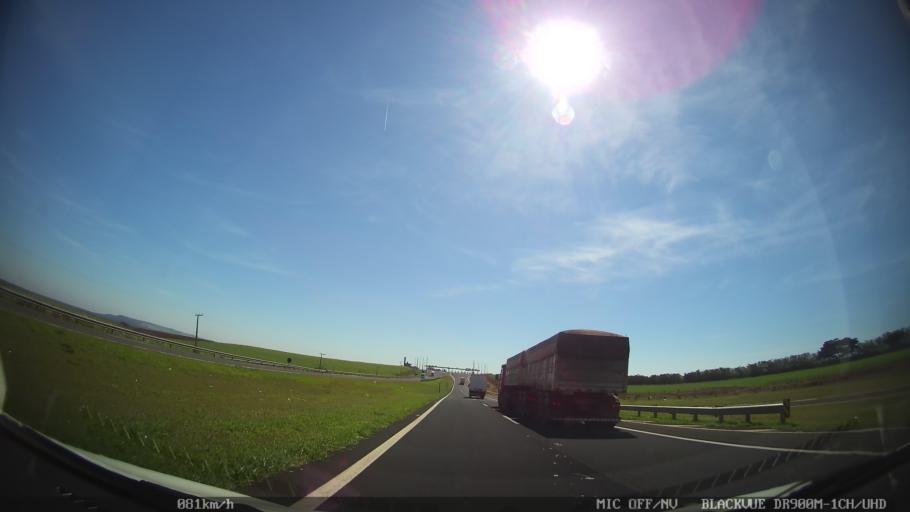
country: BR
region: Sao Paulo
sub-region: Santa Rita Do Passa Quatro
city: Santa Rita do Passa Quatro
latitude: -21.6650
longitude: -47.6078
